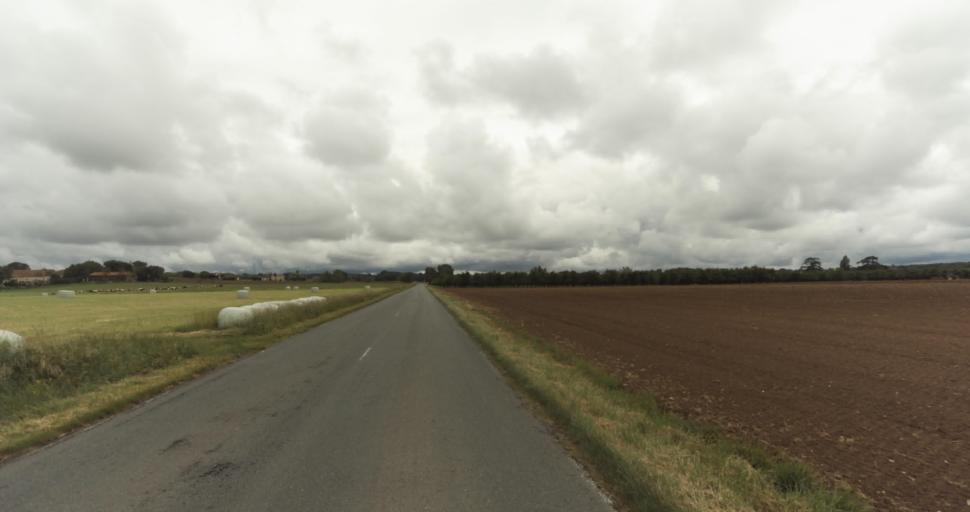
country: FR
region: Aquitaine
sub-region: Departement de la Dordogne
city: Beaumont-du-Perigord
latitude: 44.7147
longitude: 0.8055
